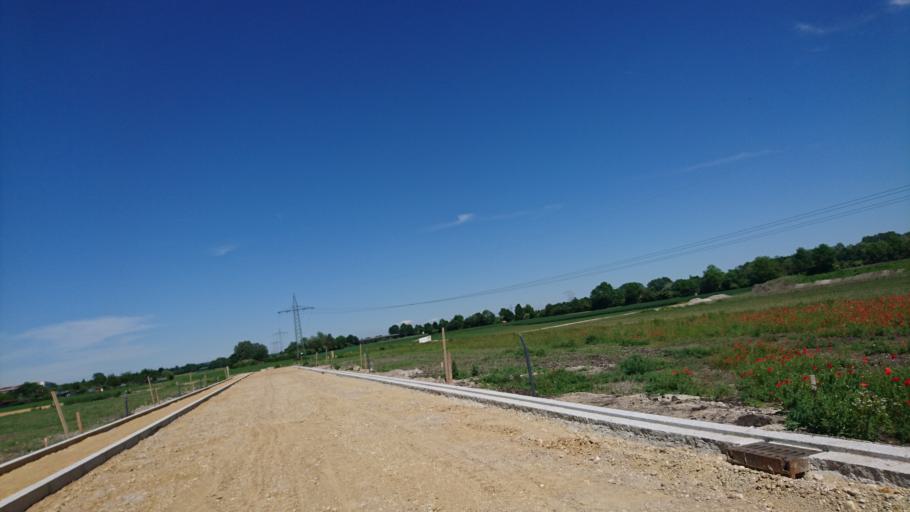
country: DE
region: Bavaria
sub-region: Lower Bavaria
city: Ergolding
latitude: 48.5696
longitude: 12.1791
